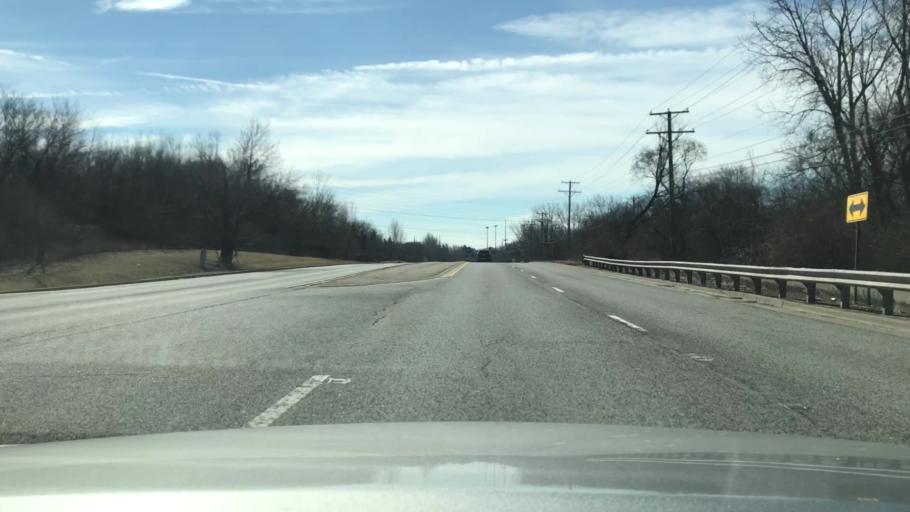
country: US
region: Illinois
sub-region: DuPage County
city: Woodridge
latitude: 41.7573
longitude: -88.0650
